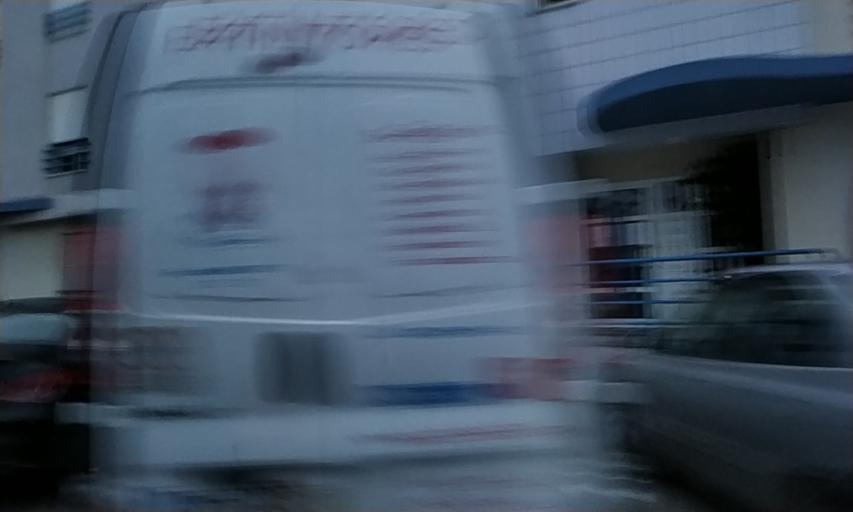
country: PT
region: Setubal
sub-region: Setubal
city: Setubal
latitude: 38.5218
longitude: -8.8505
